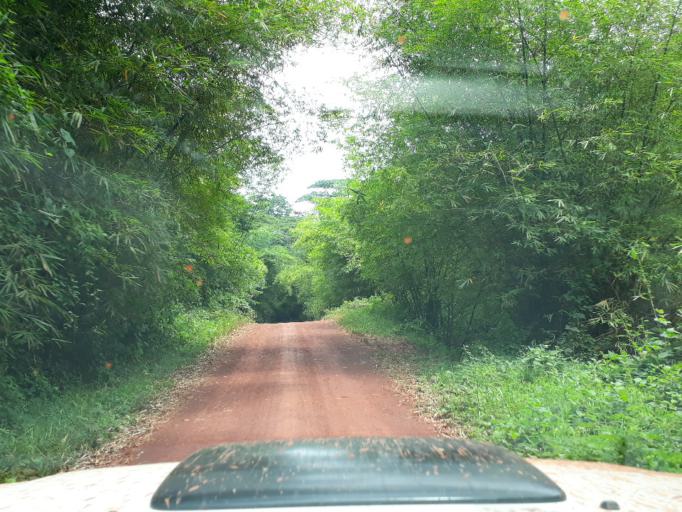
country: CD
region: Eastern Province
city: Buta
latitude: 2.5056
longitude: 24.8314
